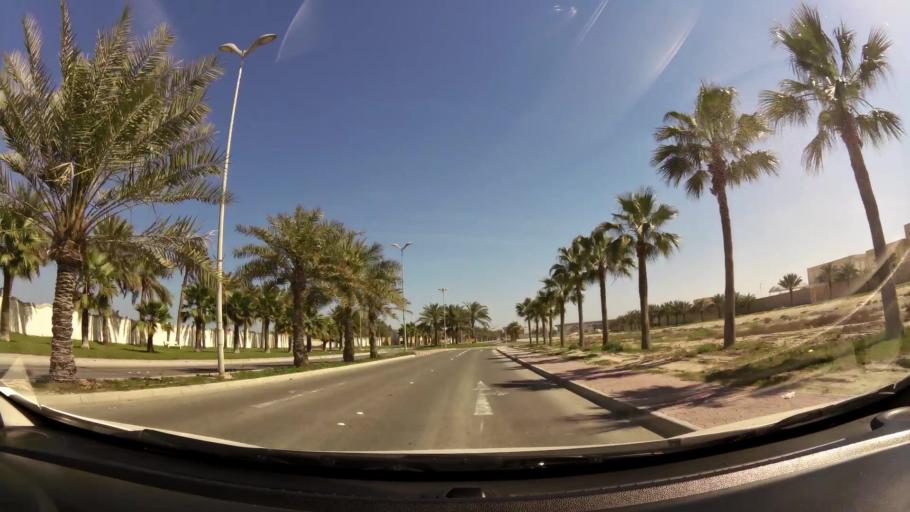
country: BH
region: Muharraq
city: Al Hadd
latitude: 26.2804
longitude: 50.6597
